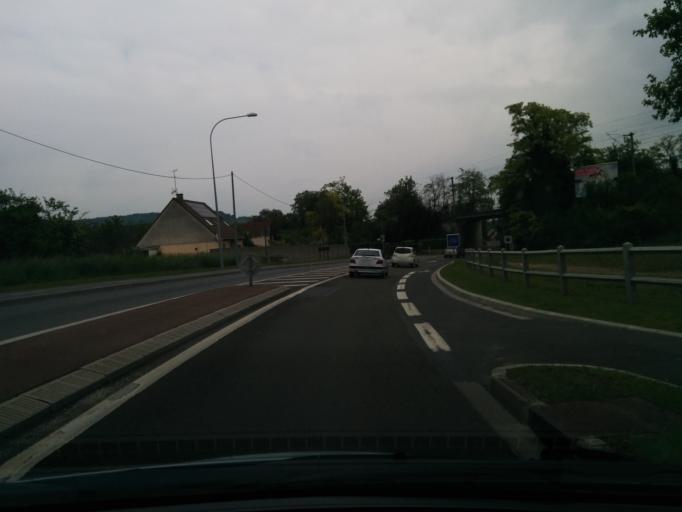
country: FR
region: Ile-de-France
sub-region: Departement des Yvelines
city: Juziers
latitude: 48.9898
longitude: 1.8347
